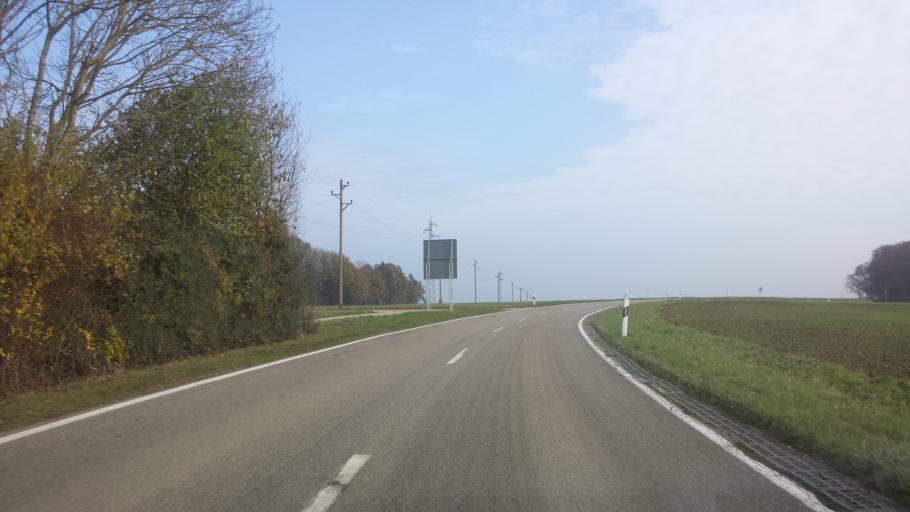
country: DE
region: Baden-Wuerttemberg
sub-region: Regierungsbezirk Stuttgart
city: Siegelsbach
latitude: 49.2586
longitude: 9.0665
